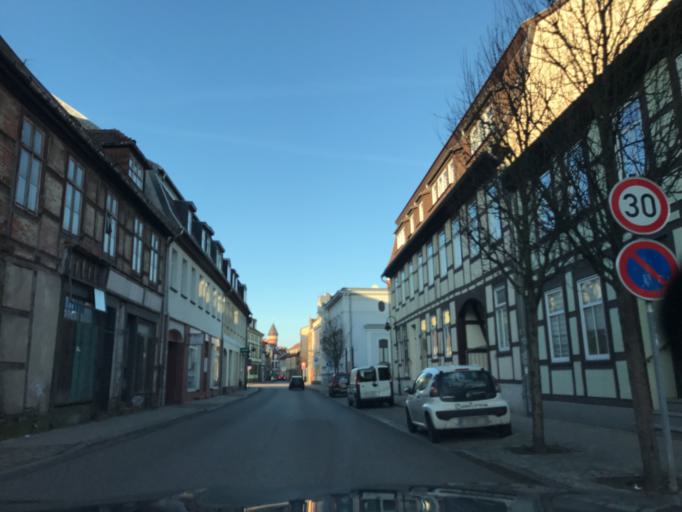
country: DE
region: Saxony-Anhalt
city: Burg bei Magdeburg
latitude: 52.2686
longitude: 11.8596
